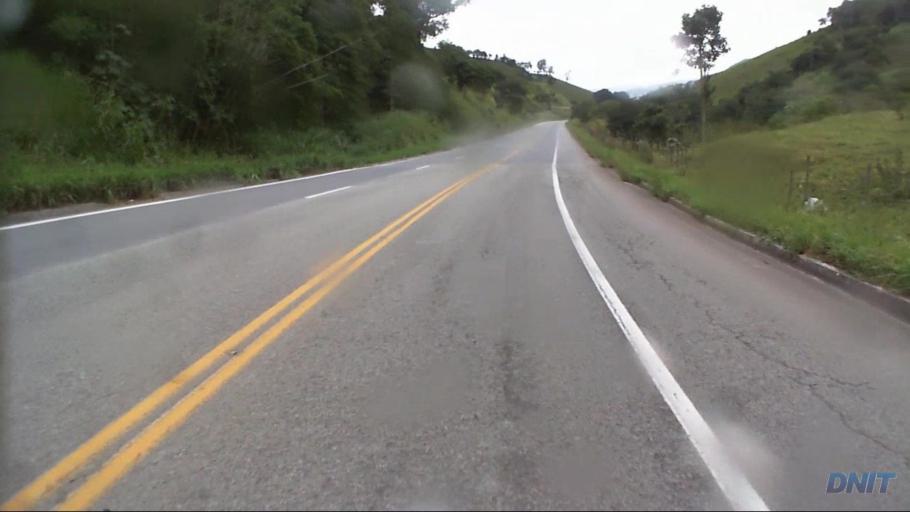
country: BR
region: Minas Gerais
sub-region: Nova Era
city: Nova Era
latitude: -19.7133
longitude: -43.0002
